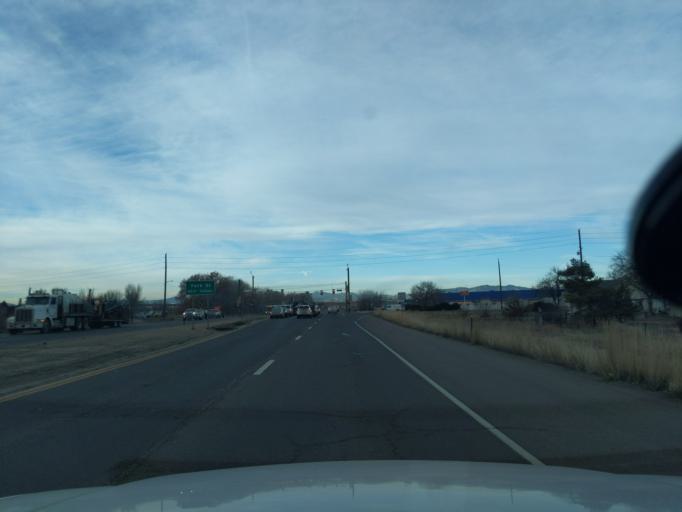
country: US
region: Colorado
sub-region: Adams County
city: Welby
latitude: 39.8294
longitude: -104.9576
